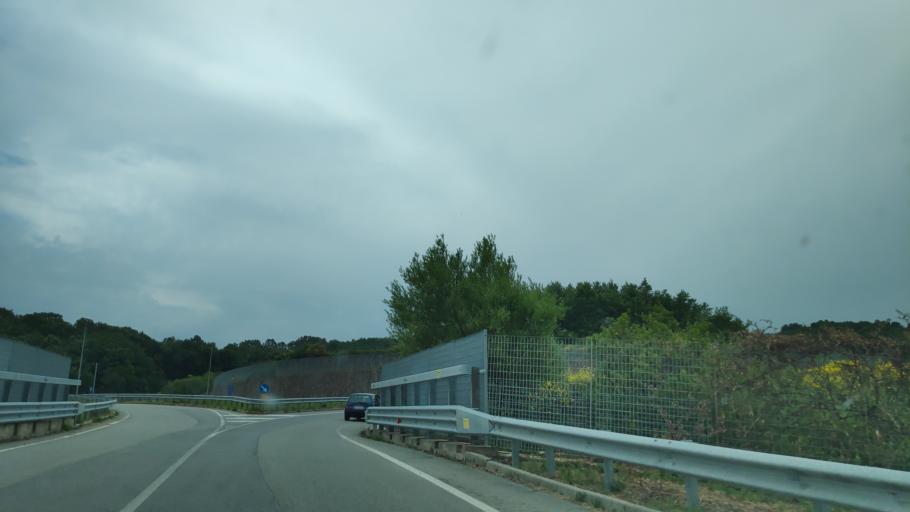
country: IT
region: Calabria
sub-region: Provincia di Catanzaro
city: Argusto
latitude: 38.6809
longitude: 16.4248
